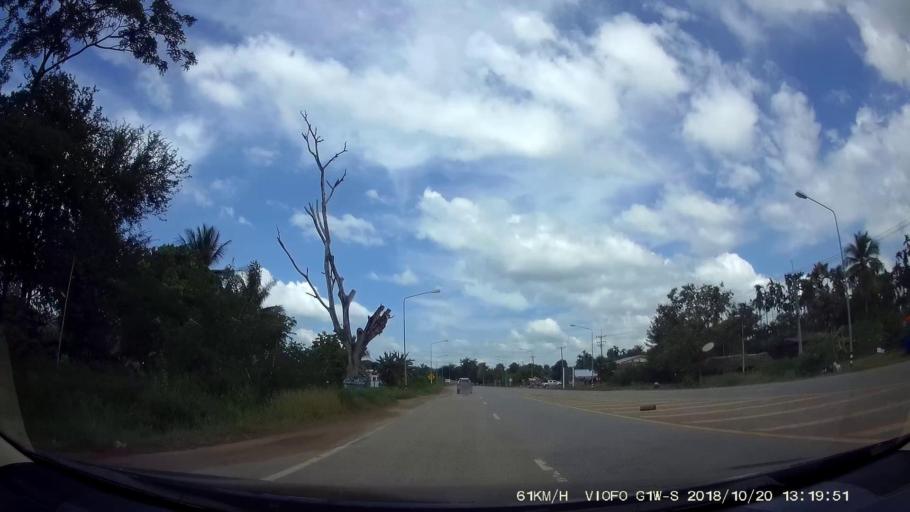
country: TH
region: Chaiyaphum
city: Khon San
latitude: 16.5425
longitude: 101.9013
